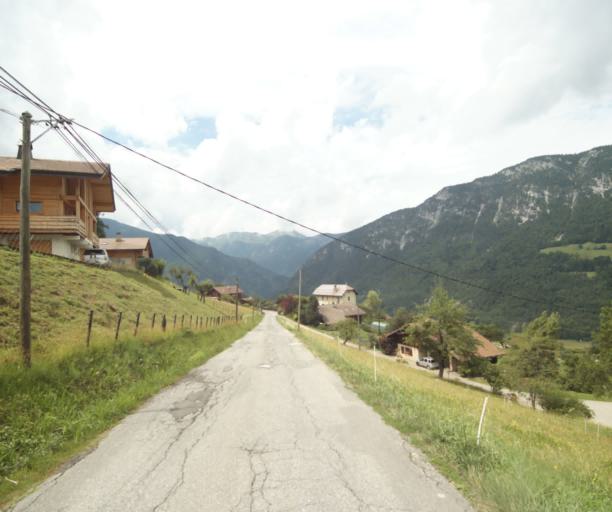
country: FR
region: Rhone-Alpes
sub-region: Departement de la Haute-Savoie
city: Thones
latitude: 45.8923
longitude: 6.3509
